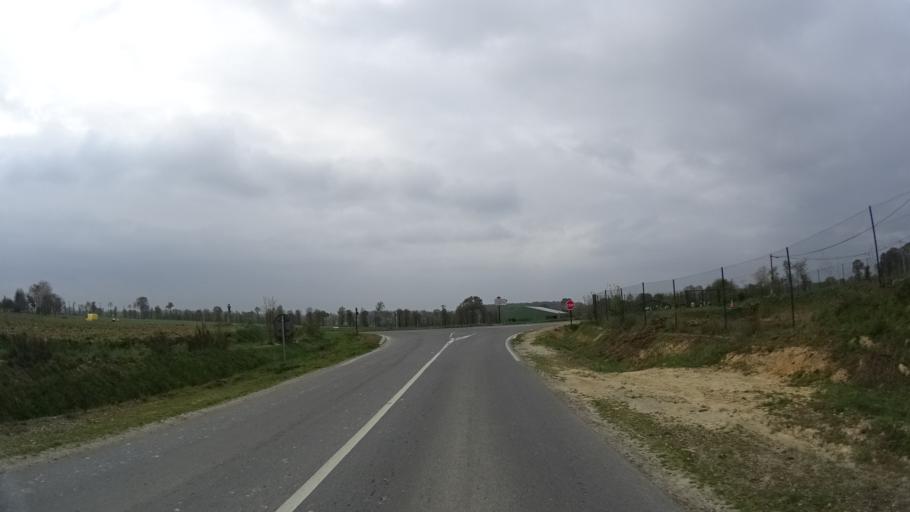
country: FR
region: Brittany
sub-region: Departement d'Ille-et-Vilaine
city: La Chapelle-Thouarault
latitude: 48.1235
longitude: -1.8542
